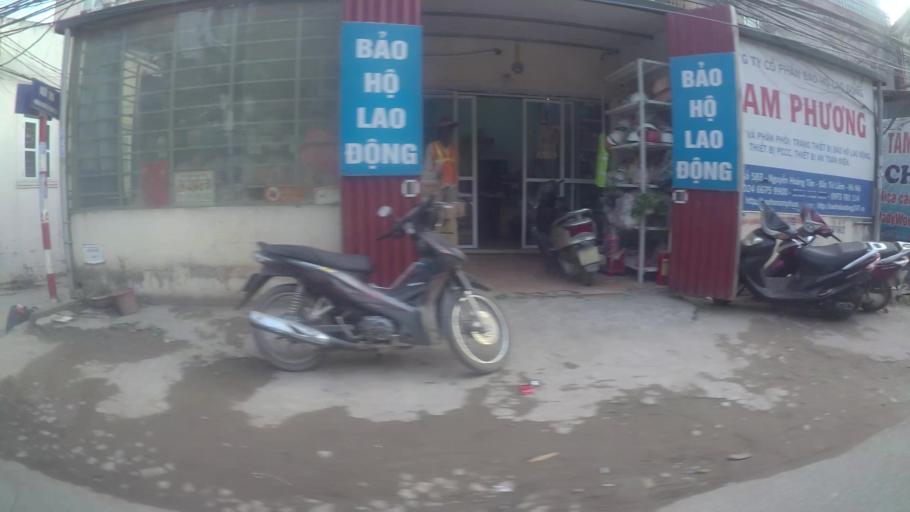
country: VN
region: Ha Noi
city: Tay Ho
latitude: 21.0763
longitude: 105.7936
